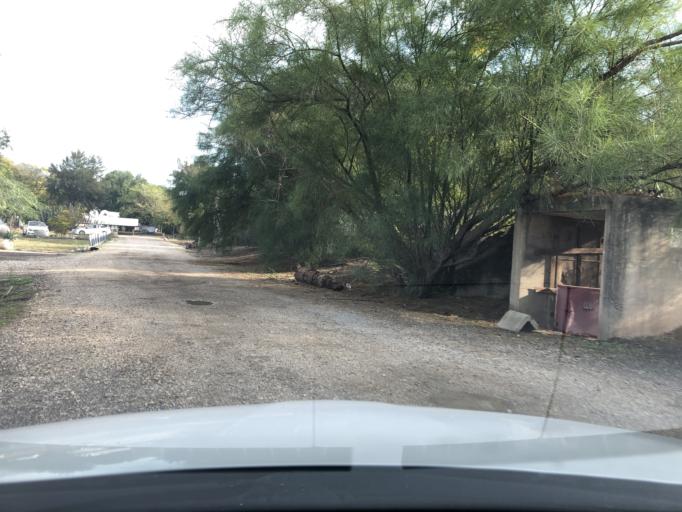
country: IL
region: Northern District
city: Yavne'el
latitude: 32.6596
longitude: 35.5827
